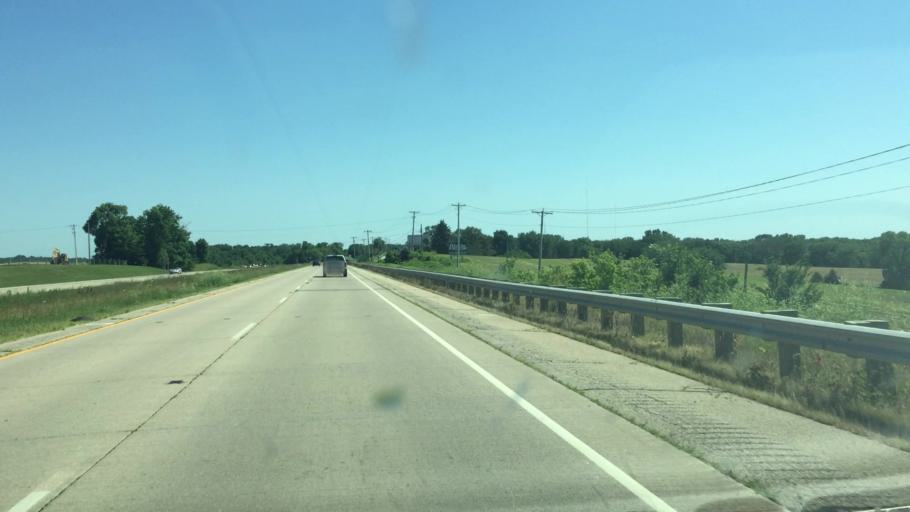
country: US
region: Wisconsin
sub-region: Grant County
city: Dickeyville
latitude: 42.5617
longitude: -90.6109
